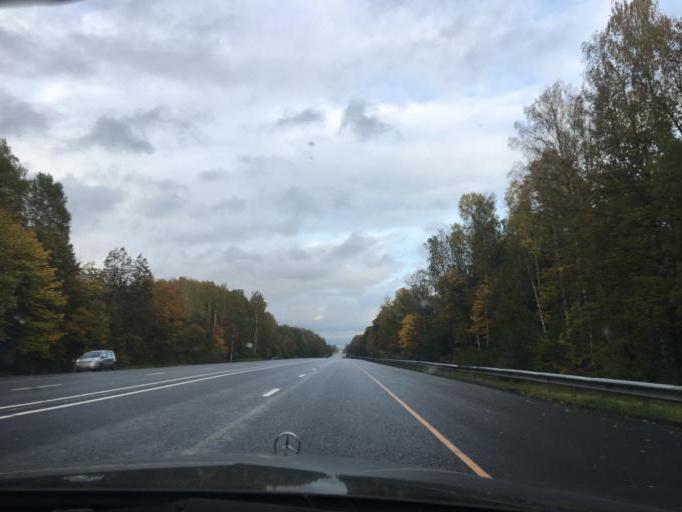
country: RU
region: Smolensk
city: Katyn'
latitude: 54.8467
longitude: 31.7411
